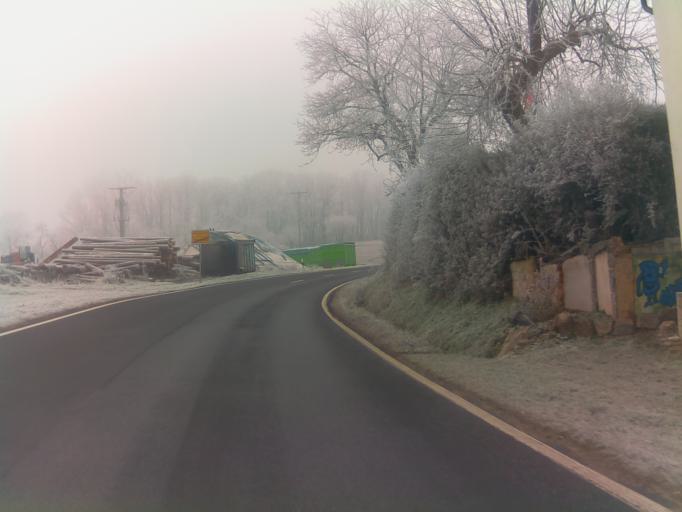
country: DE
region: Bavaria
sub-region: Regierungsbezirk Unterfranken
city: Wonfurt
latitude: 49.9969
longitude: 10.4579
